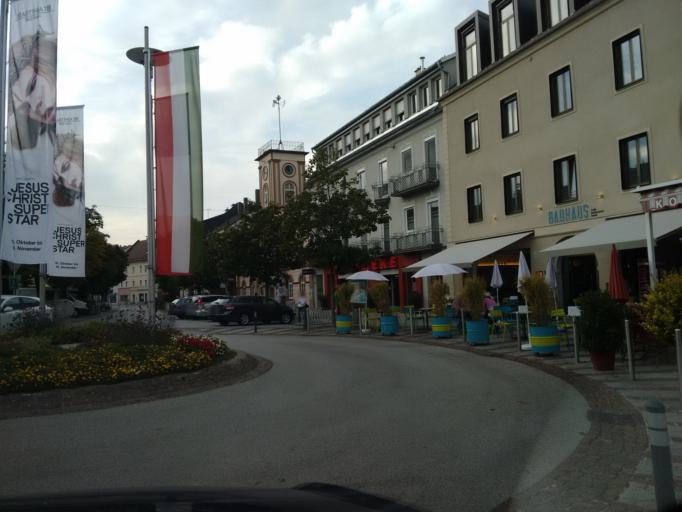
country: AT
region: Upper Austria
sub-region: Politischer Bezirk Steyr-Land
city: Bad Hall
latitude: 48.0348
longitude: 14.2089
